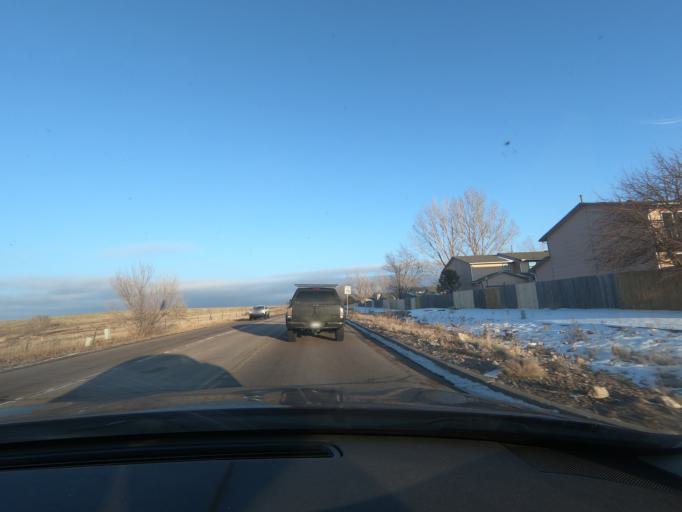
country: US
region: Colorado
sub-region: El Paso County
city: Security-Widefield
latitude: 38.7374
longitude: -104.7049
